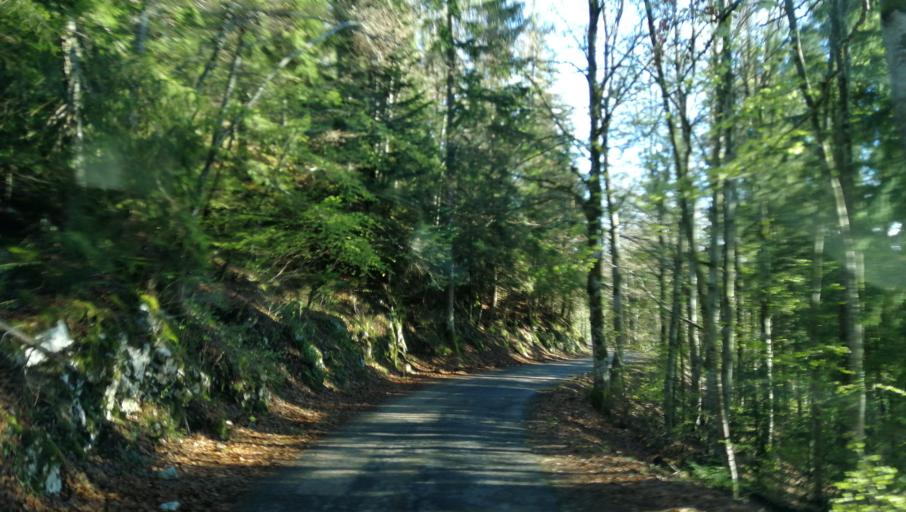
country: FR
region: Rhone-Alpes
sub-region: Departement de l'Ain
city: Chatillon-en-Michaille
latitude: 46.2583
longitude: 5.7967
